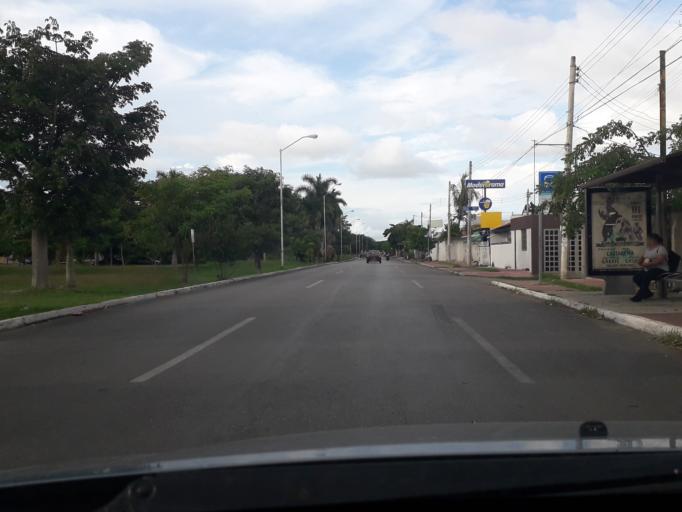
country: MX
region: Yucatan
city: Merida
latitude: 20.9766
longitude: -89.6631
